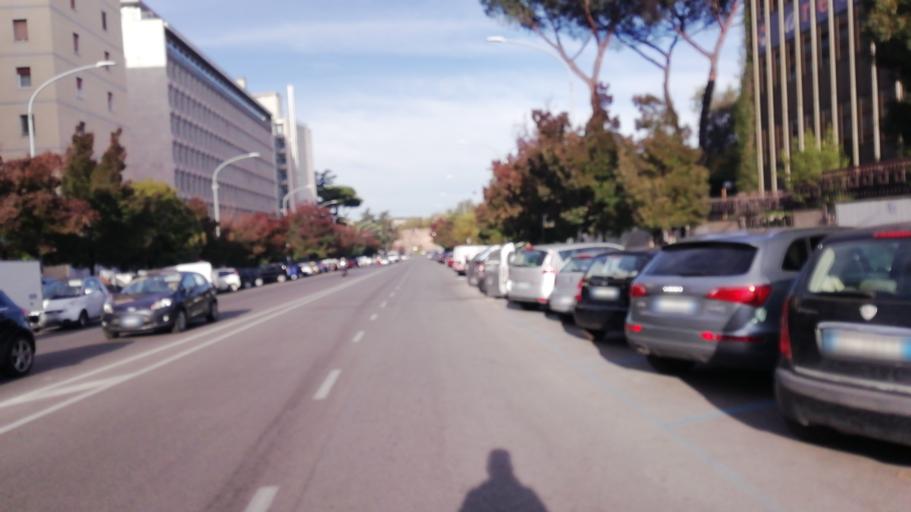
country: IT
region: Latium
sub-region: Citta metropolitana di Roma Capitale
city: Rome
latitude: 41.8748
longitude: 12.4856
